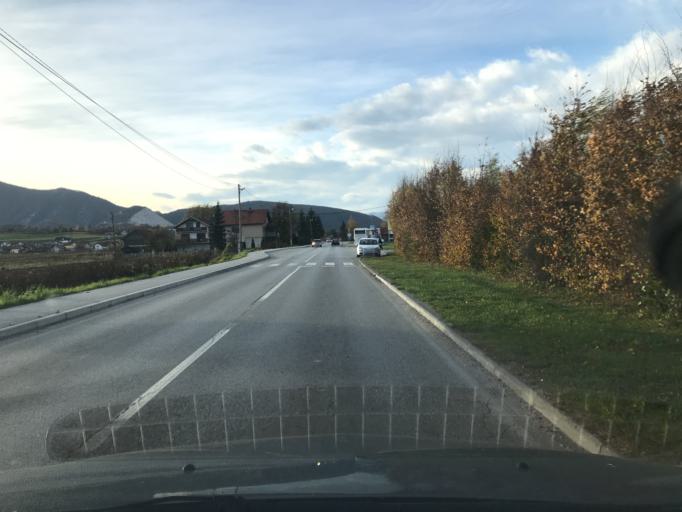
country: BA
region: Federation of Bosnia and Herzegovina
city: Vitez
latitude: 44.1638
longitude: 17.7759
